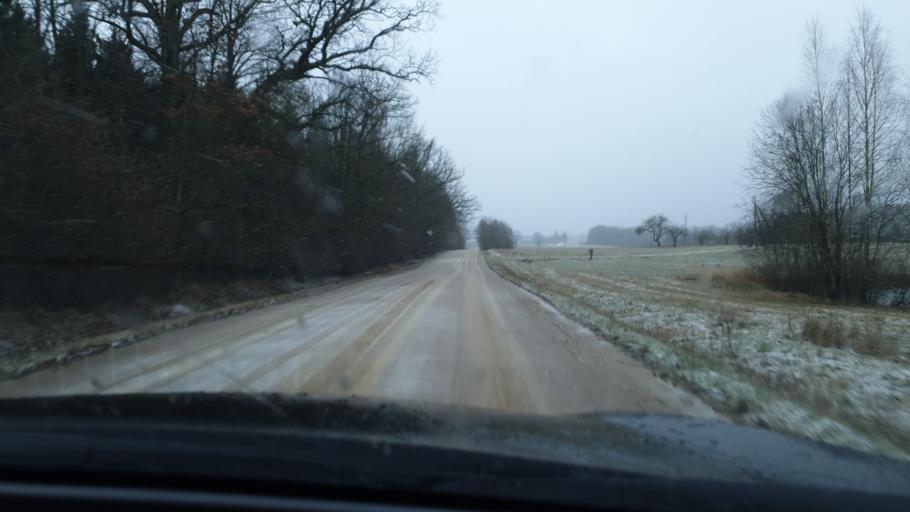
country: LT
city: Jieznas
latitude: 54.5650
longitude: 24.3179
